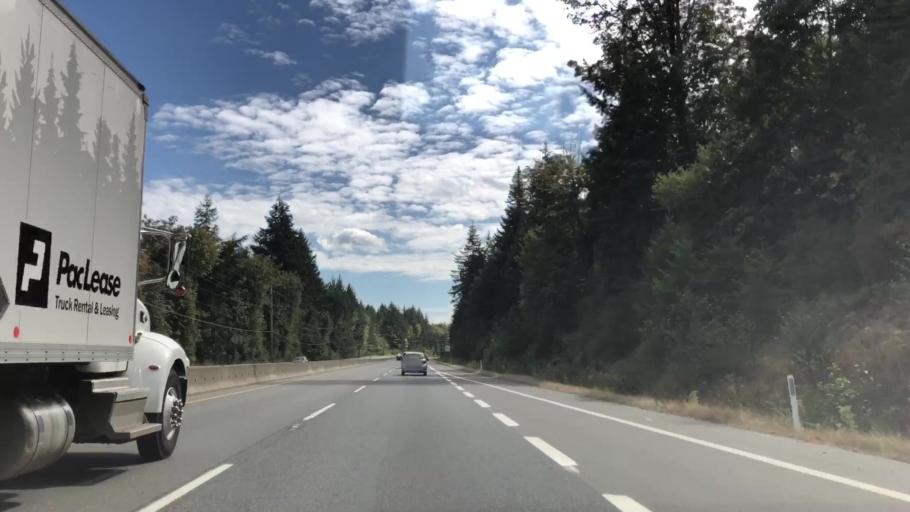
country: CA
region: British Columbia
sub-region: Cowichan Valley Regional District
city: Ladysmith
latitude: 48.9302
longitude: -123.7549
